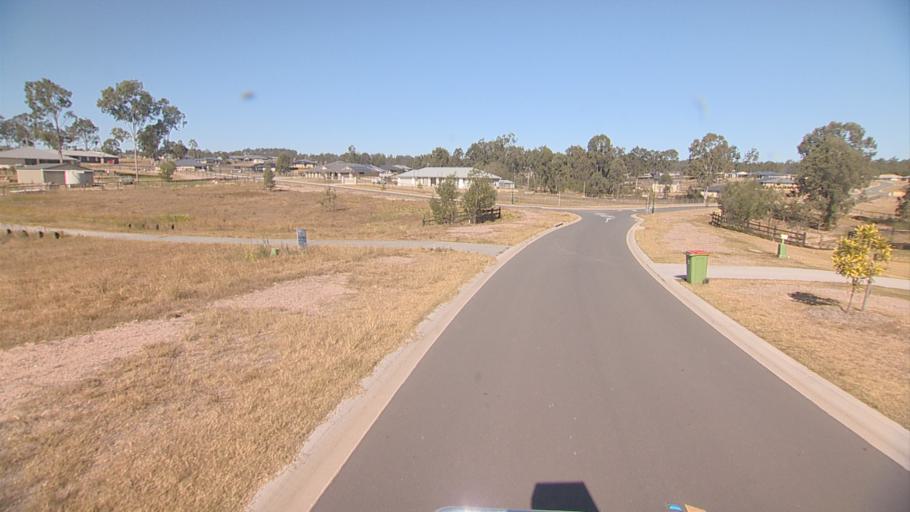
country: AU
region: Queensland
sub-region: Logan
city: Cedar Vale
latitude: -27.8643
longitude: 153.0438
